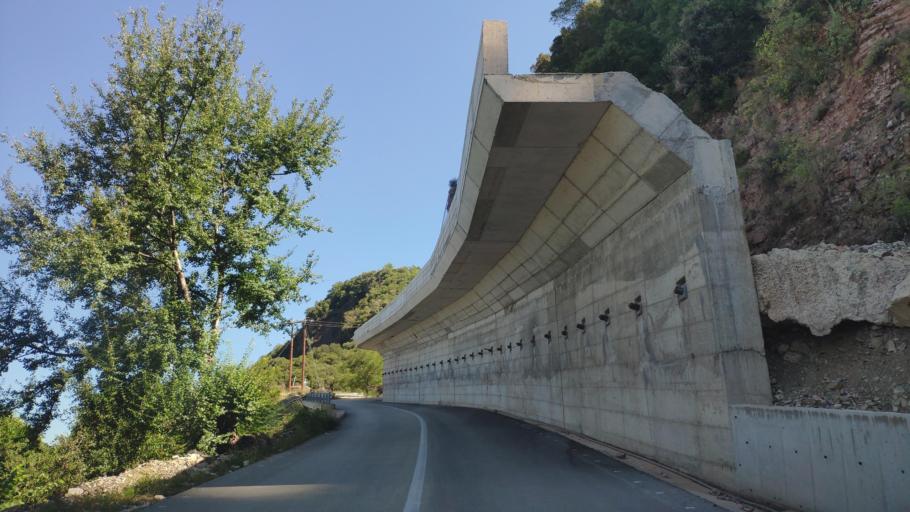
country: GR
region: Central Greece
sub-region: Nomos Evrytanias
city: Kerasochori
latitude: 39.0042
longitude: 21.5888
